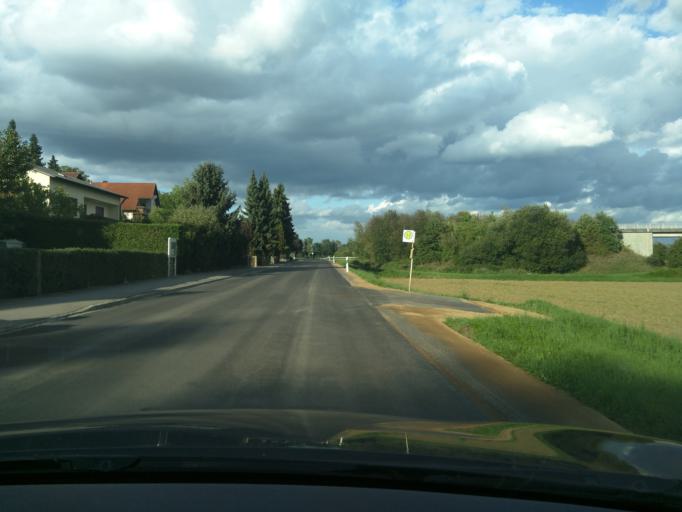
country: DE
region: Bavaria
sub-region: Upper Palatinate
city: Schwandorf in Bayern
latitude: 49.3442
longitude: 12.0936
